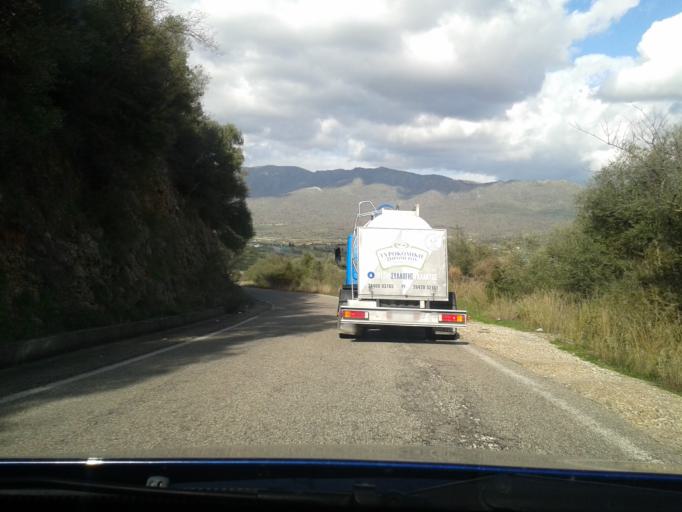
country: GR
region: West Greece
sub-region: Nomos Aitolias kai Akarnanias
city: Fitiai
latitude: 38.6848
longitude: 21.2109
